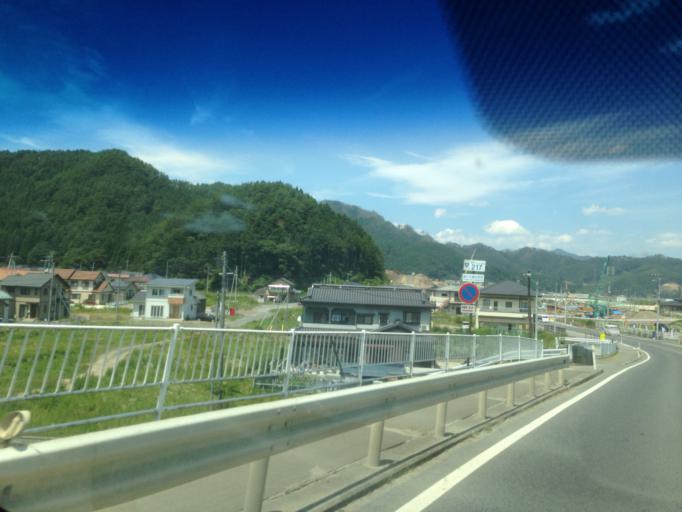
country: JP
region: Iwate
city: Kamaishi
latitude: 39.3208
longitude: 141.8837
